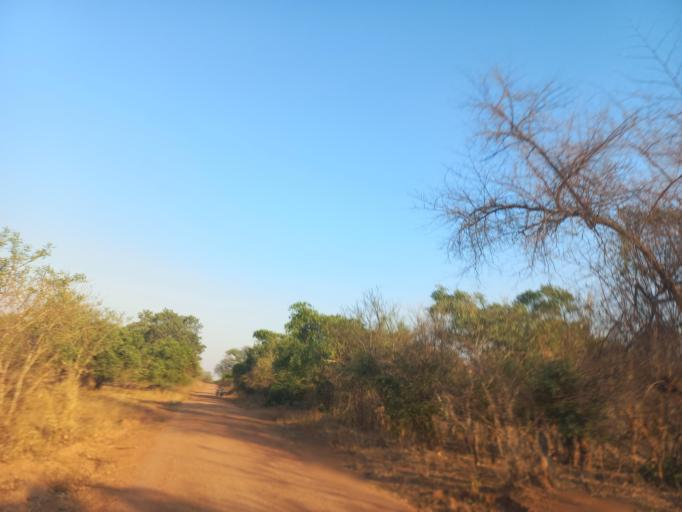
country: ZM
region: Lusaka
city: Luangwa
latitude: -15.4367
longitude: 30.3539
